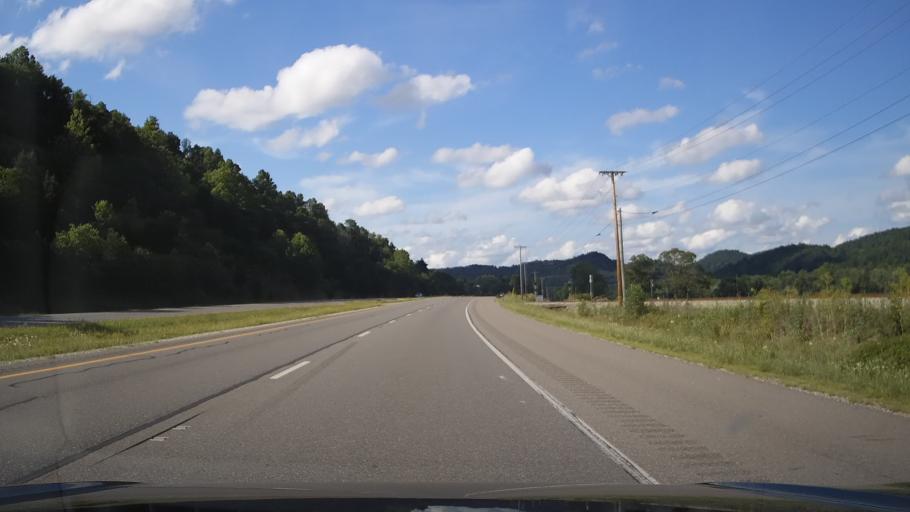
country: US
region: Kentucky
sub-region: Lawrence County
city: Louisa
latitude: 38.1993
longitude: -82.6042
